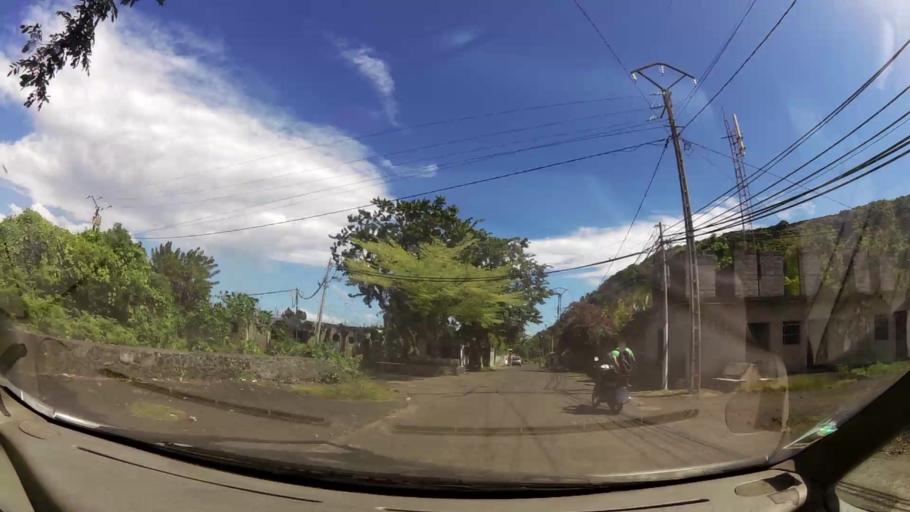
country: KM
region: Grande Comore
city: Mavingouni
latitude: -11.7415
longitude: 43.2391
